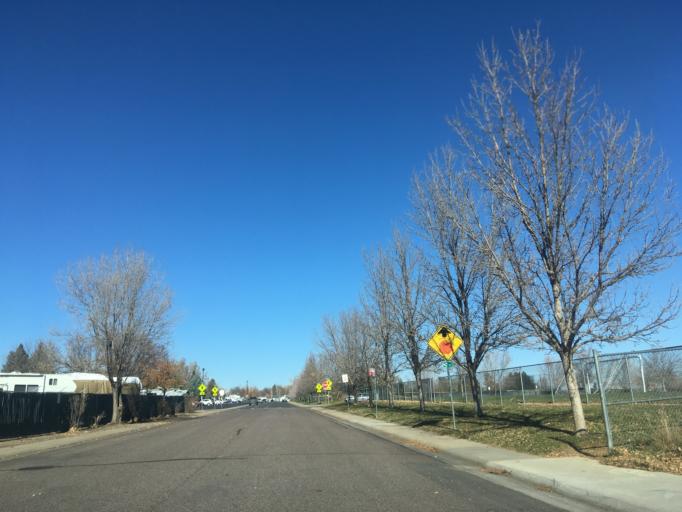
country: US
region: Colorado
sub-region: Boulder County
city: Lafayette
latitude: 39.9905
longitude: -105.0811
